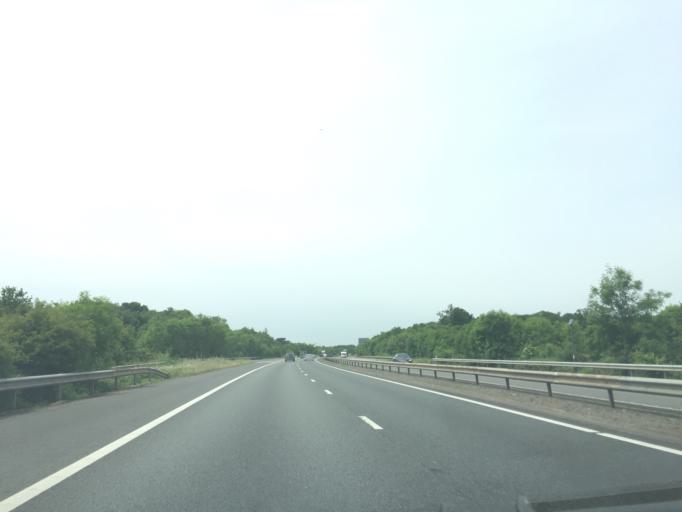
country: GB
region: England
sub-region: Kent
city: Borough Green
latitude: 51.3009
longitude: 0.3295
